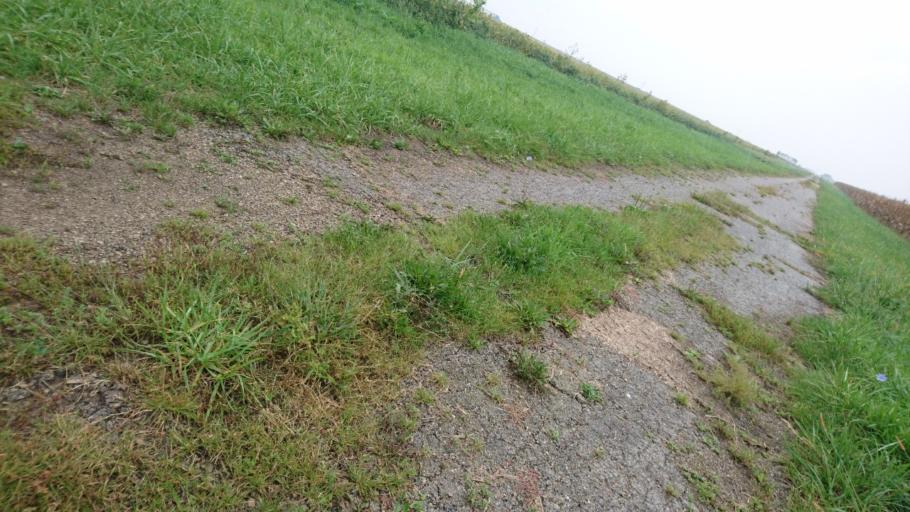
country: US
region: Illinois
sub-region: Logan County
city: Lincoln
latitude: 40.1069
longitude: -89.4111
